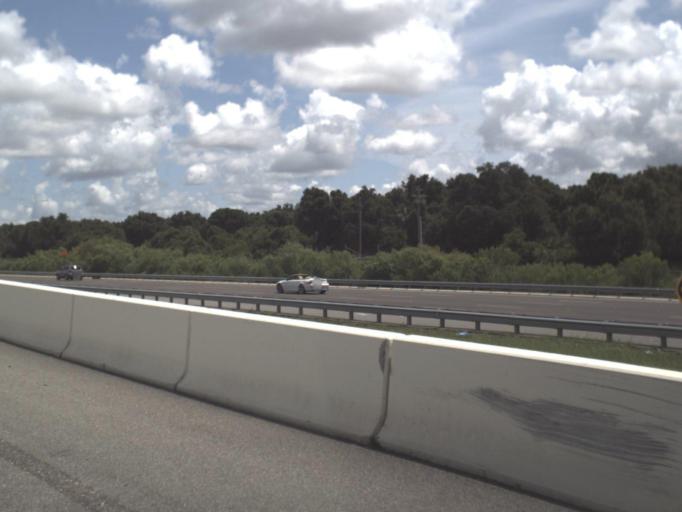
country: US
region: Florida
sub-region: Hillsborough County
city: Town 'n' Country
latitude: 27.9741
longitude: -82.5464
